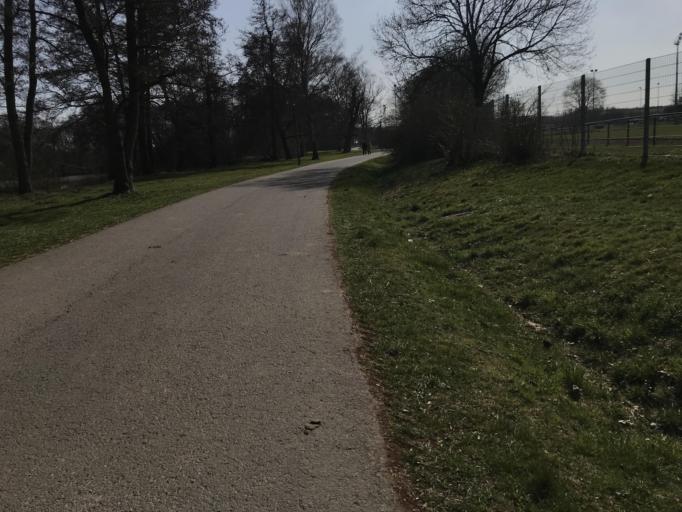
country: DE
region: Hesse
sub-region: Regierungsbezirk Kassel
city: Fulda
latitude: 50.5415
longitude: 9.6690
